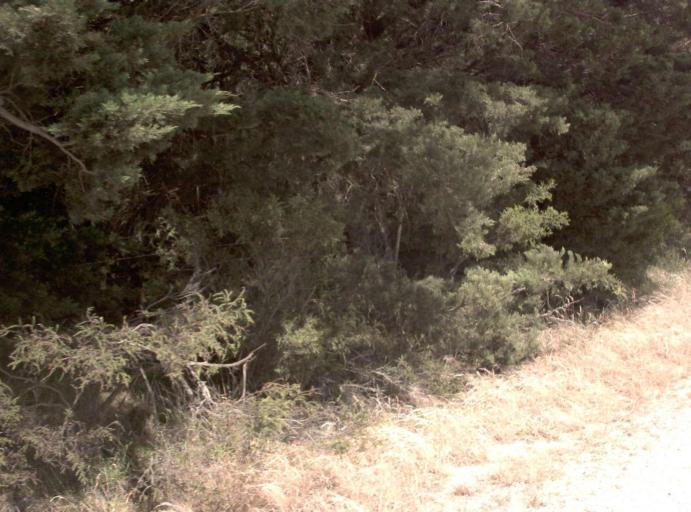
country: AU
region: Victoria
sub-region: Wellington
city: Heyfield
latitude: -38.0300
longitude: 146.8794
